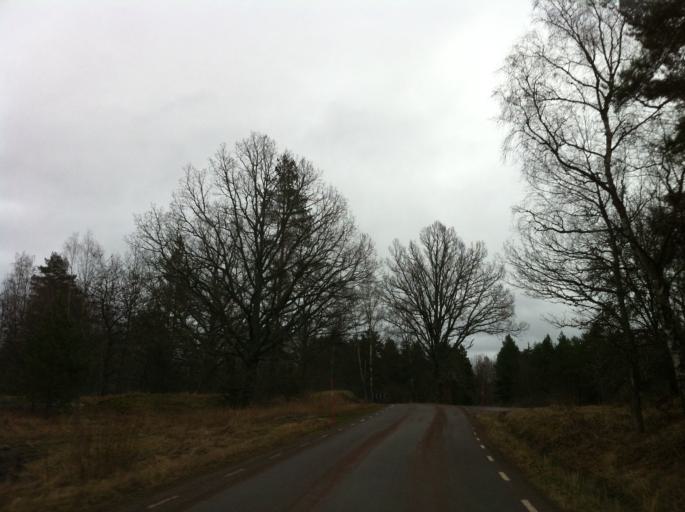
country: SE
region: Kalmar
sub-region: Vasterviks Kommun
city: Forserum
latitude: 57.9220
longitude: 16.5675
